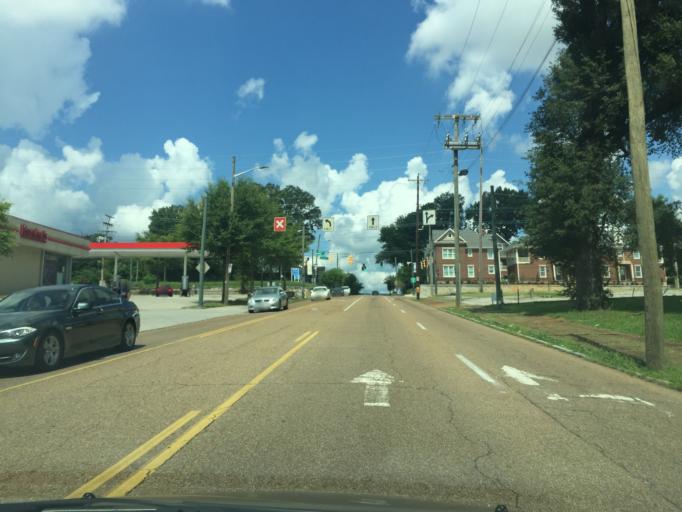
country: US
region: Tennessee
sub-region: Hamilton County
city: Chattanooga
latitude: 35.0416
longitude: -85.2900
